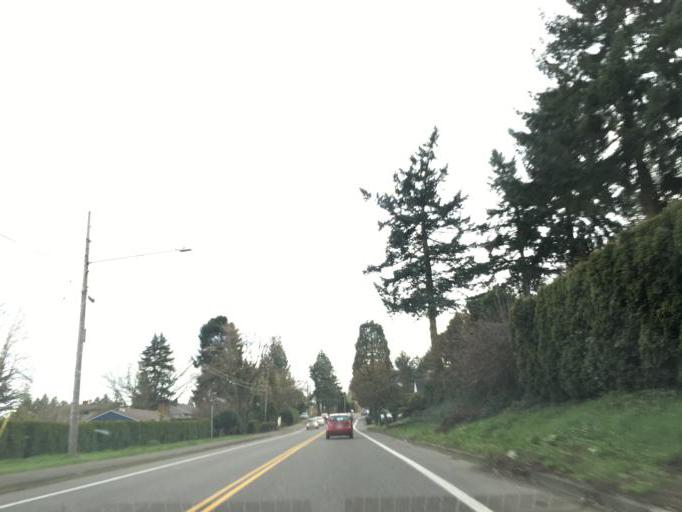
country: US
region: Oregon
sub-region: Clackamas County
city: Lake Oswego
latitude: 45.4660
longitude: -122.6835
